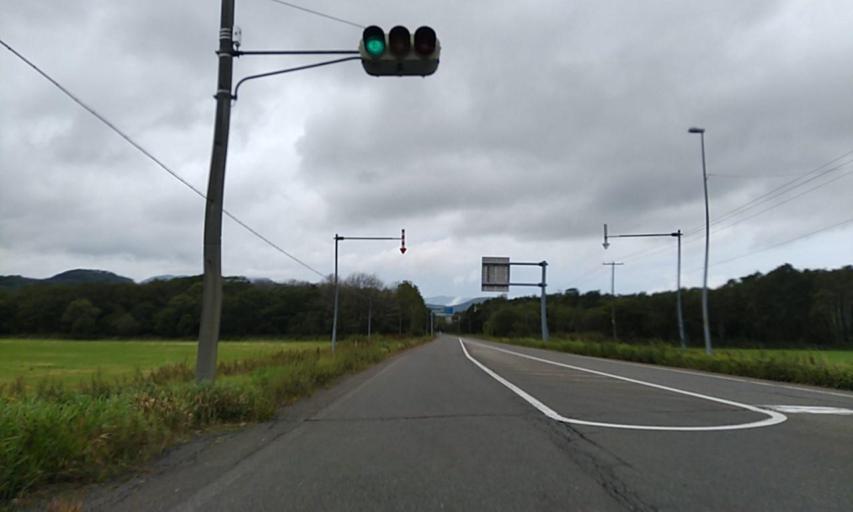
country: JP
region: Hokkaido
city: Bihoro
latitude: 43.5161
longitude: 144.4300
